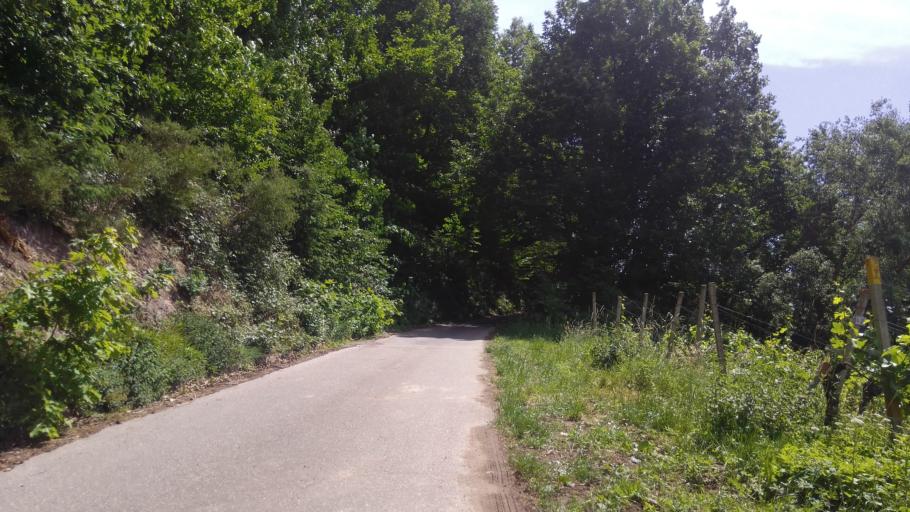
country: DE
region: Baden-Wuerttemberg
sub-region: Karlsruhe Region
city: Sinzheim
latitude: 48.7396
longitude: 8.1892
